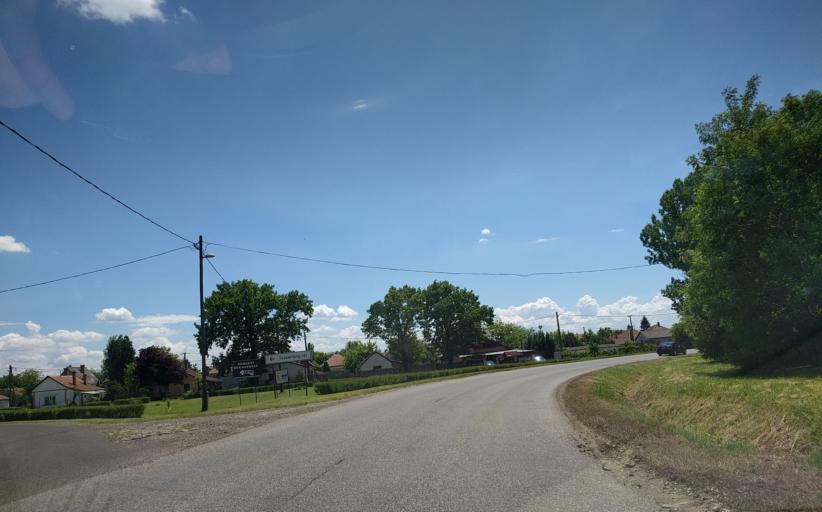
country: HU
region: Jasz-Nagykun-Szolnok
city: Toszeg
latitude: 47.0692
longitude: 20.1763
